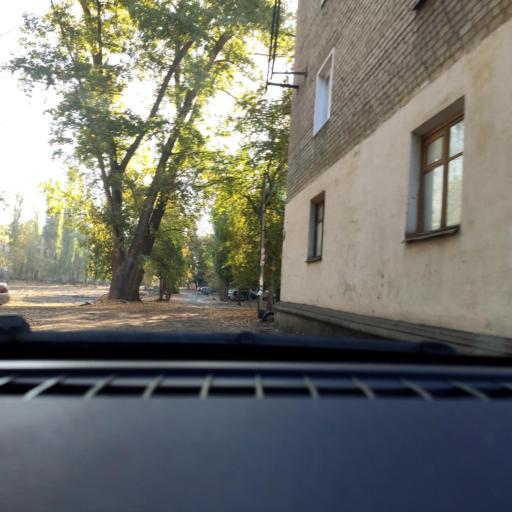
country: RU
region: Voronezj
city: Maslovka
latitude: 51.6140
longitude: 39.2526
